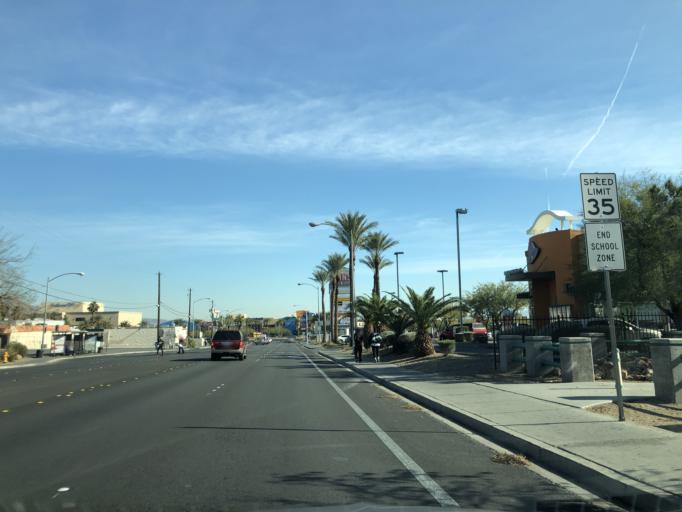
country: US
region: Nevada
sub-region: Clark County
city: Winchester
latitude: 36.1221
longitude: -115.1398
